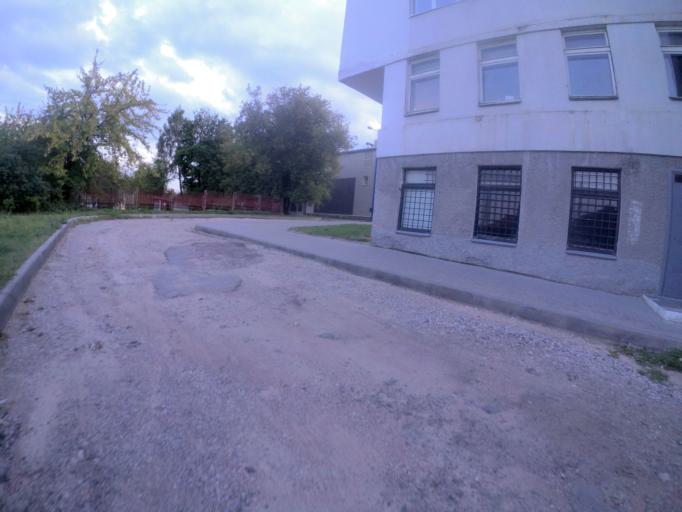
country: BY
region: Grodnenskaya
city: Hrodna
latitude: 53.6919
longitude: 23.8259
